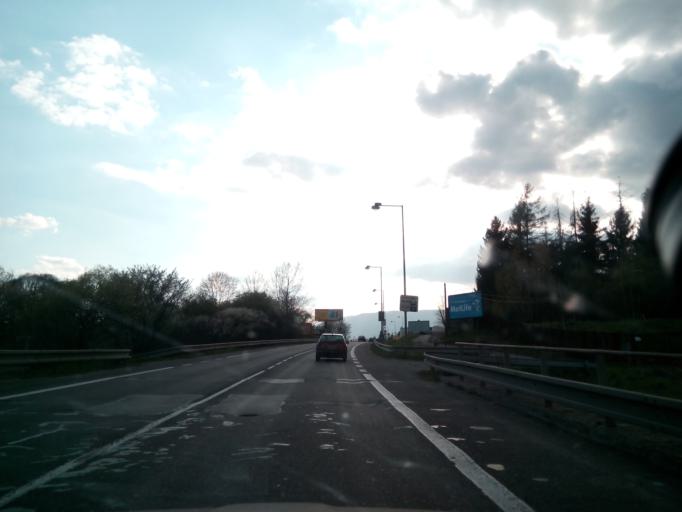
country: SK
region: Zilinsky
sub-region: Okres Zilina
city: Vrutky
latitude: 49.1075
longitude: 19.0056
